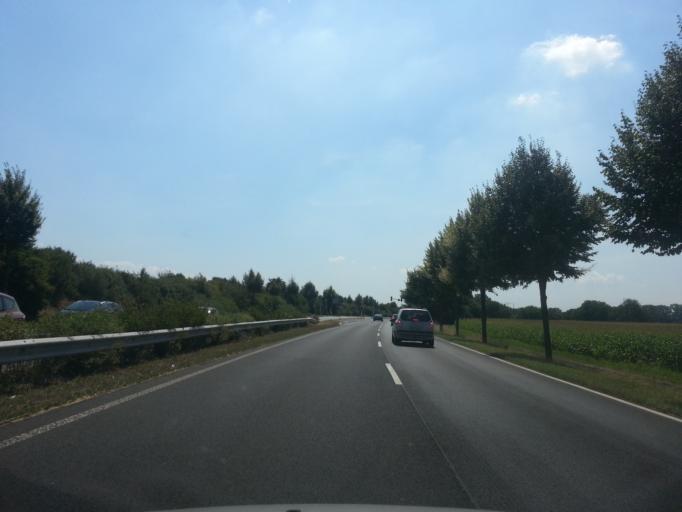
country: DE
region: Hesse
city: Lampertheim
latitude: 49.5666
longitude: 8.4478
